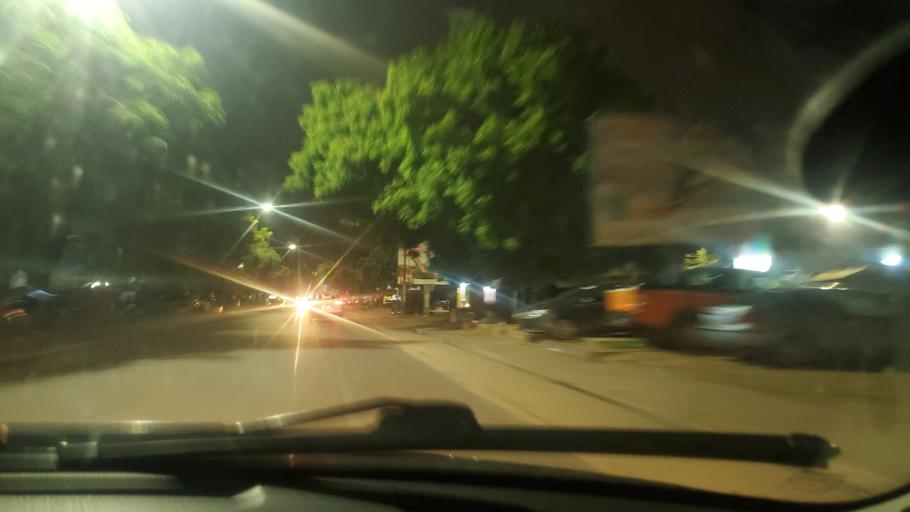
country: SN
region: Dakar
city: Grand Dakar
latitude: 14.7196
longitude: -17.4491
